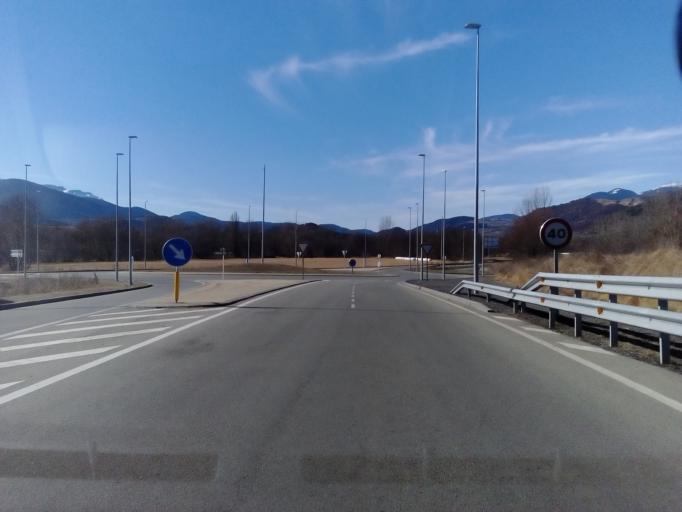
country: ES
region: Catalonia
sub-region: Provincia de Lleida
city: Bellver de Cerdanya
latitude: 42.3703
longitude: 1.8006
